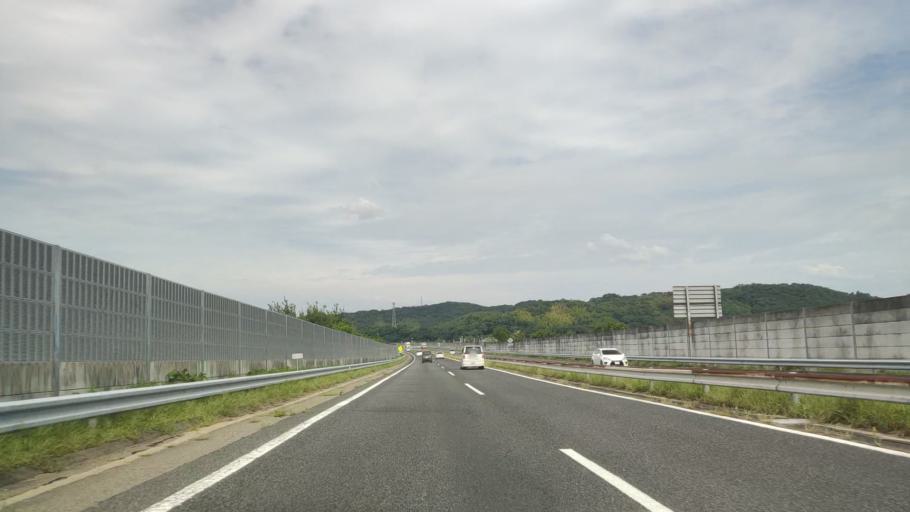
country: JP
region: Wakayama
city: Kainan
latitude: 34.1675
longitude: 135.2339
